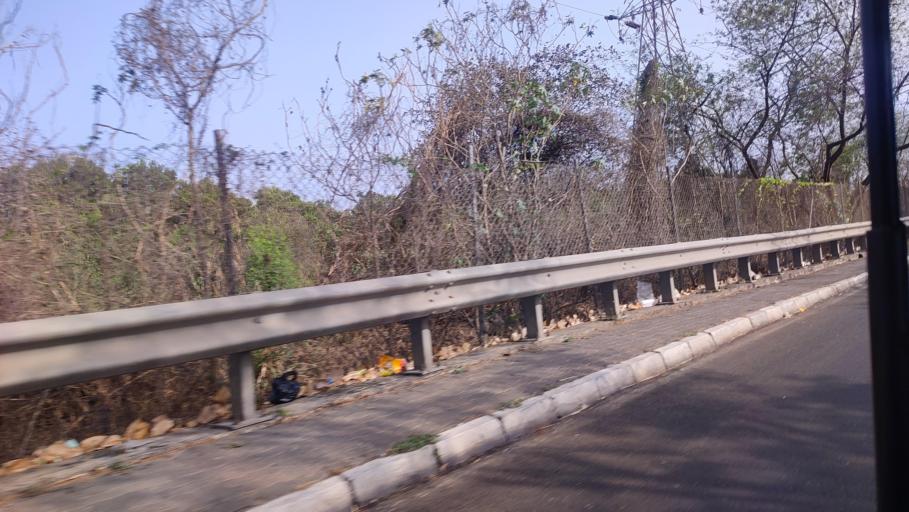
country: IN
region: Maharashtra
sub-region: Mumbai Suburban
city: Powai
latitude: 19.0872
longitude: 72.9237
